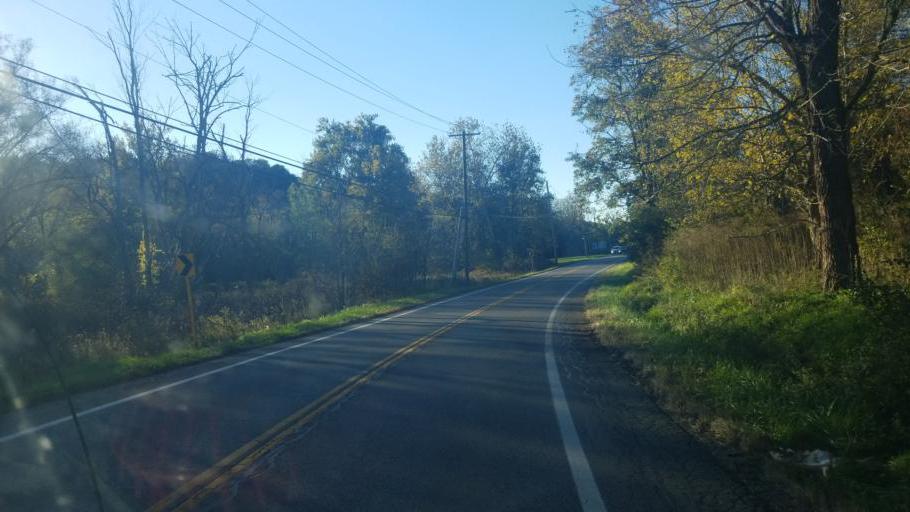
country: US
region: Ohio
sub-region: Columbiana County
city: Leetonia
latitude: 40.9036
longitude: -80.8001
